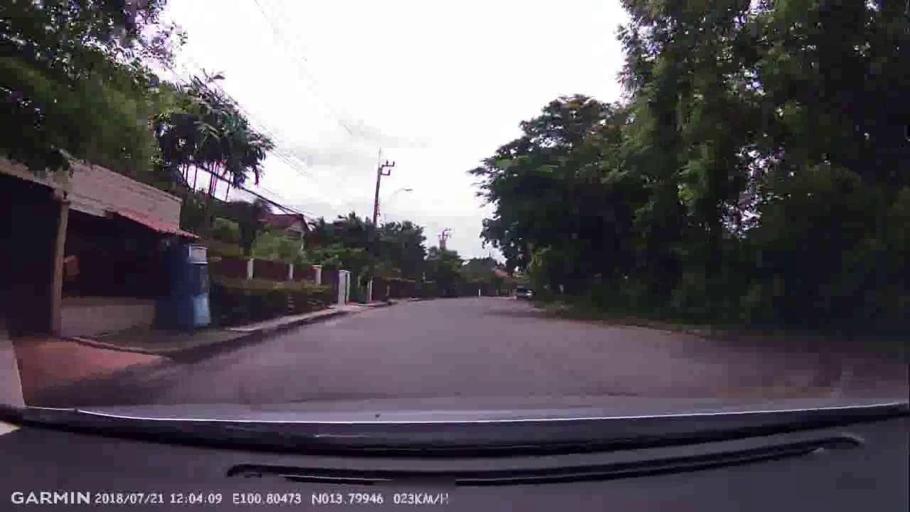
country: TH
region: Bangkok
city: Min Buri
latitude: 13.7994
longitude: 100.8048
